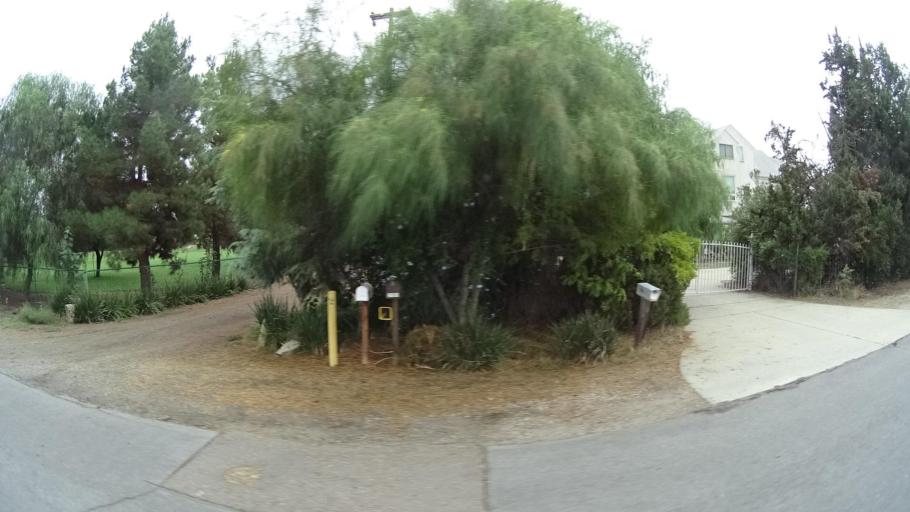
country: US
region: California
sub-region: San Diego County
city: Ramona
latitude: 33.0462
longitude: -116.8995
